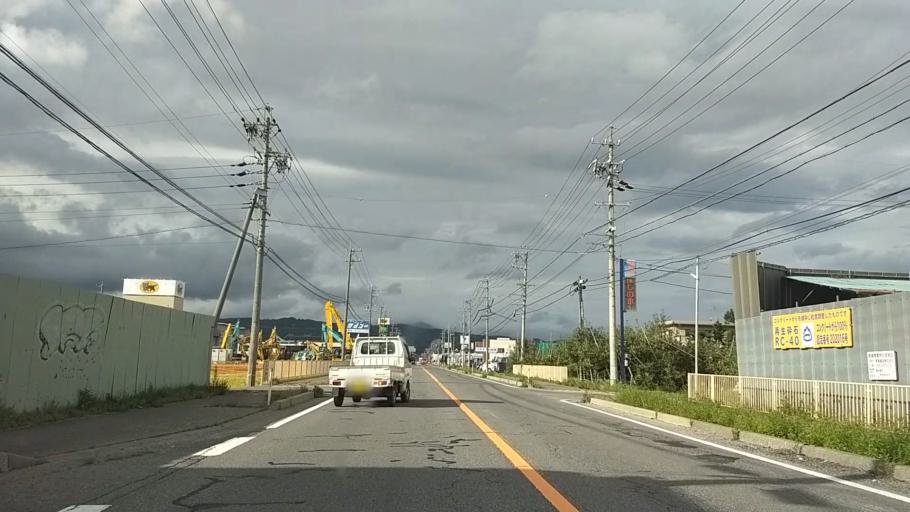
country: JP
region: Nagano
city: Suzaka
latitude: 36.6797
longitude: 138.2677
